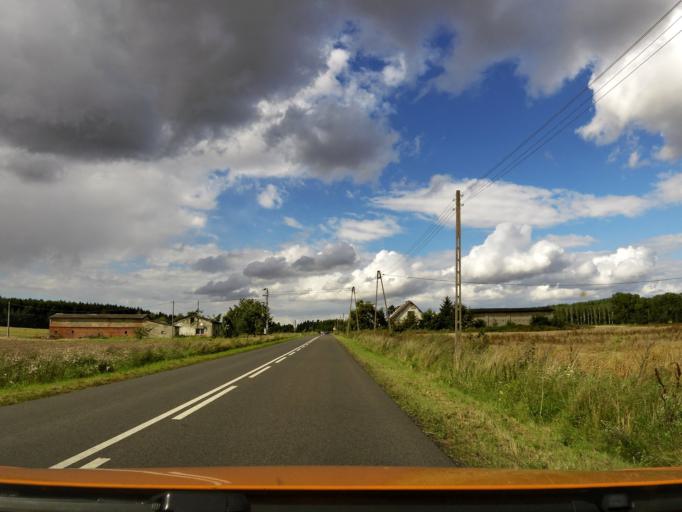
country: PL
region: West Pomeranian Voivodeship
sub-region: Powiat kolobrzeski
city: Ryman
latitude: 53.9744
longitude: 15.4900
